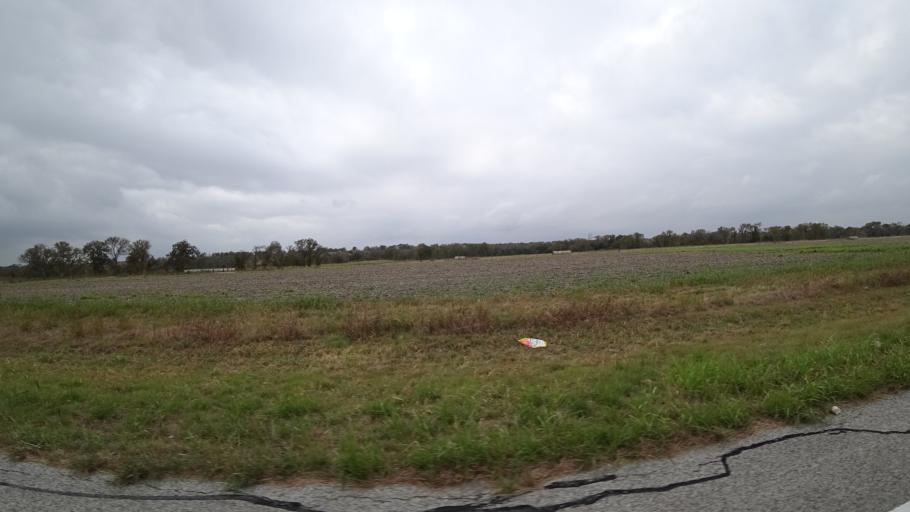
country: US
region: Texas
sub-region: Travis County
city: Pflugerville
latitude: 30.4388
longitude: -97.5928
